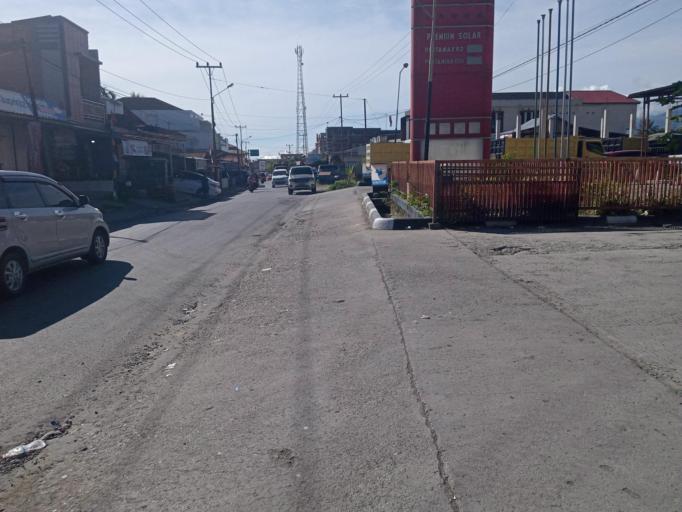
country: ID
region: Jambi
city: Semurup
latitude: -1.9520
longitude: 101.3379
